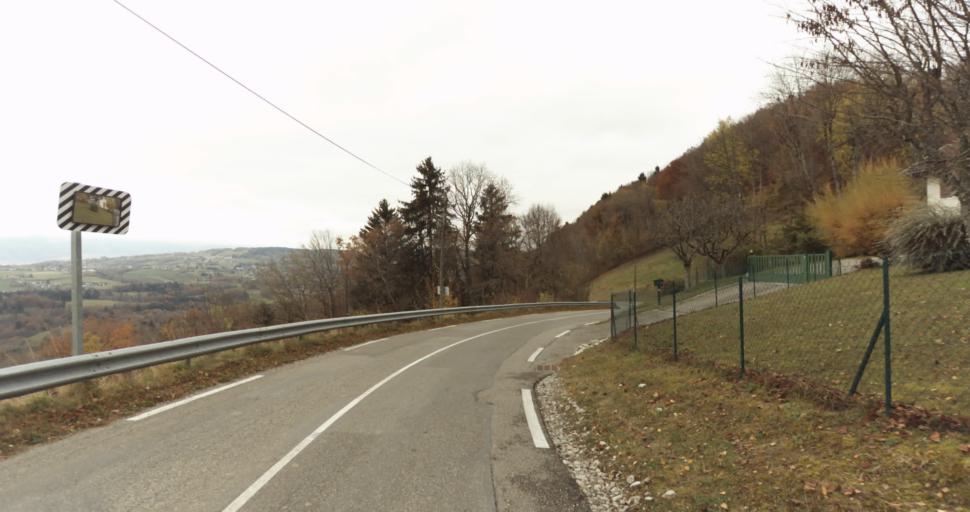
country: FR
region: Rhone-Alpes
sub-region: Departement de la Haute-Savoie
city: Saint-Martin-Bellevue
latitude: 45.9838
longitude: 6.1793
